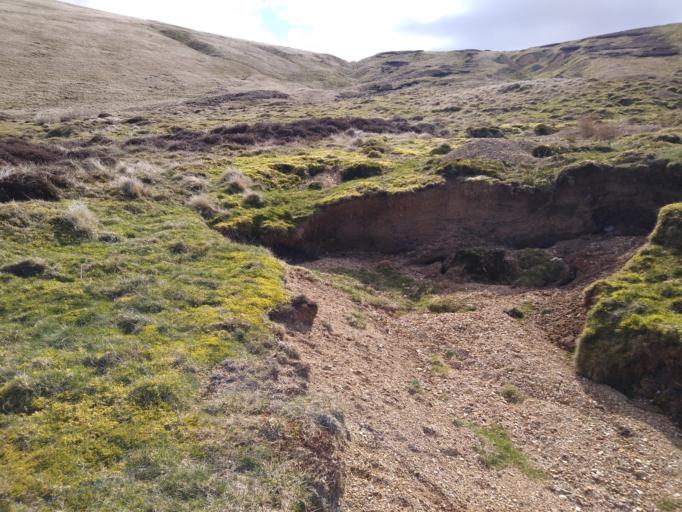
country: GB
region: England
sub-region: Cumbria
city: Keswick
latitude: 54.7050
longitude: -3.0676
